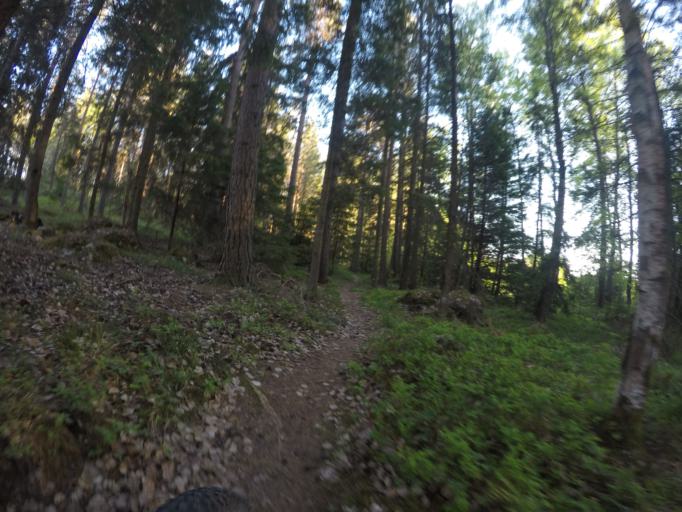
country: SE
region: Soedermanland
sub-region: Eskilstuna Kommun
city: Eskilstuna
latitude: 59.3300
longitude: 16.5253
